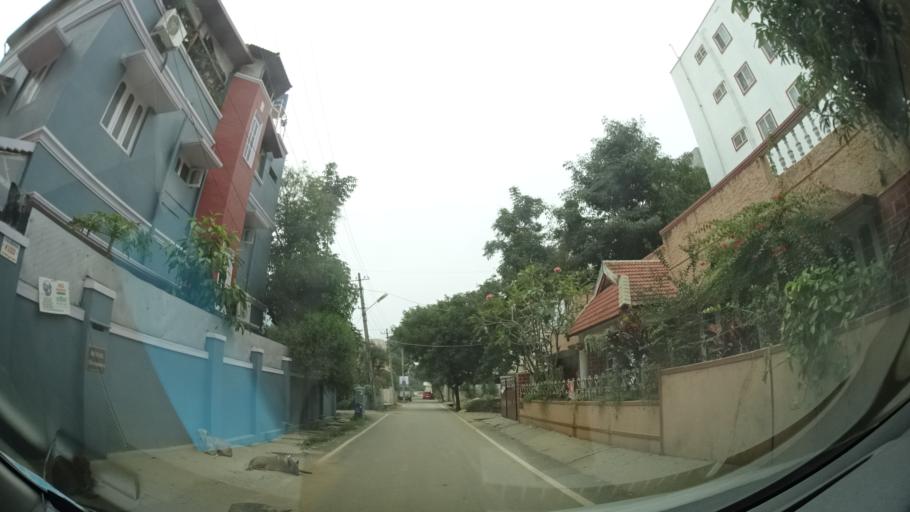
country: IN
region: Karnataka
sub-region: Bangalore Rural
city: Hoskote
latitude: 12.9835
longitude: 77.7498
